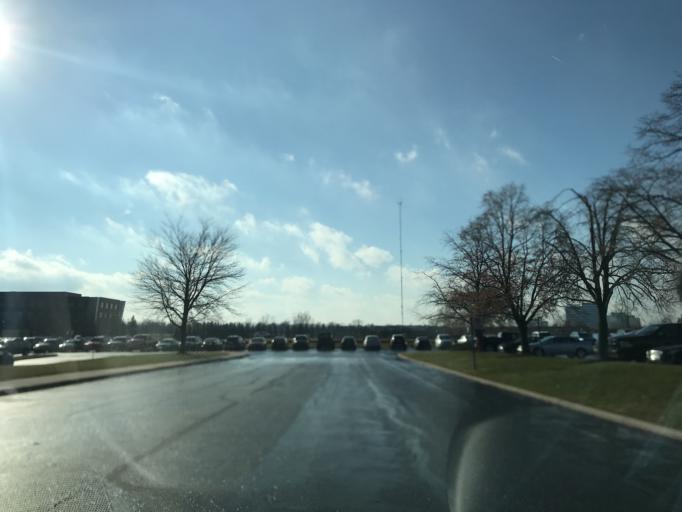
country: US
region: Michigan
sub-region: Oakland County
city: Franklin
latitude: 42.4906
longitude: -83.2999
